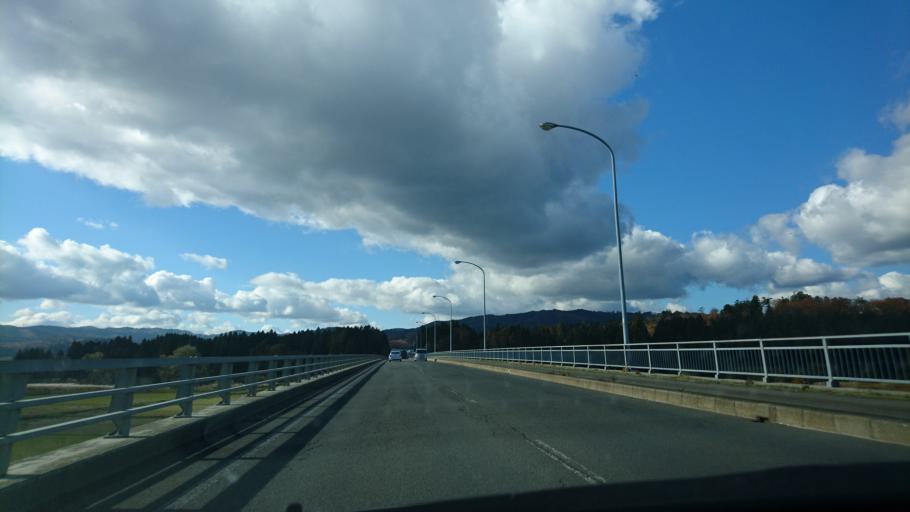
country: JP
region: Akita
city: Yuzawa
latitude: 39.2757
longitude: 140.4034
